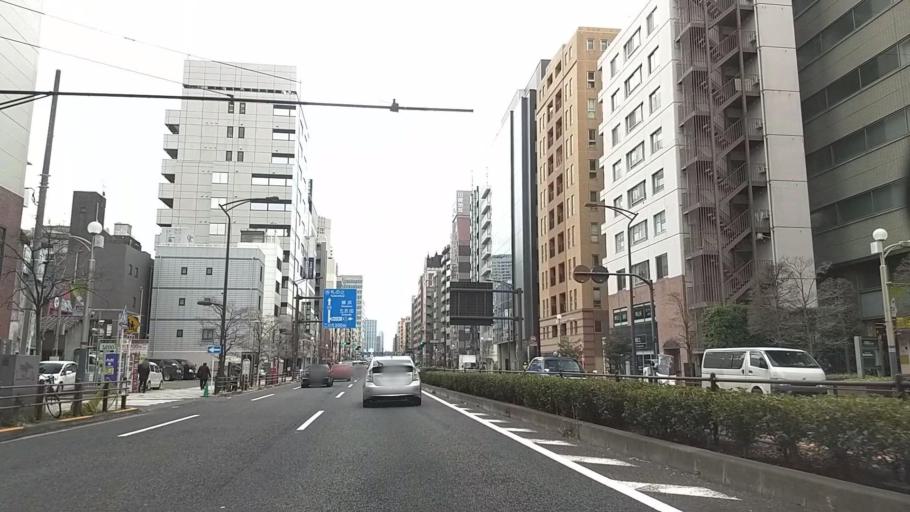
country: JP
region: Tokyo
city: Tokyo
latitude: 35.6517
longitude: 139.7450
